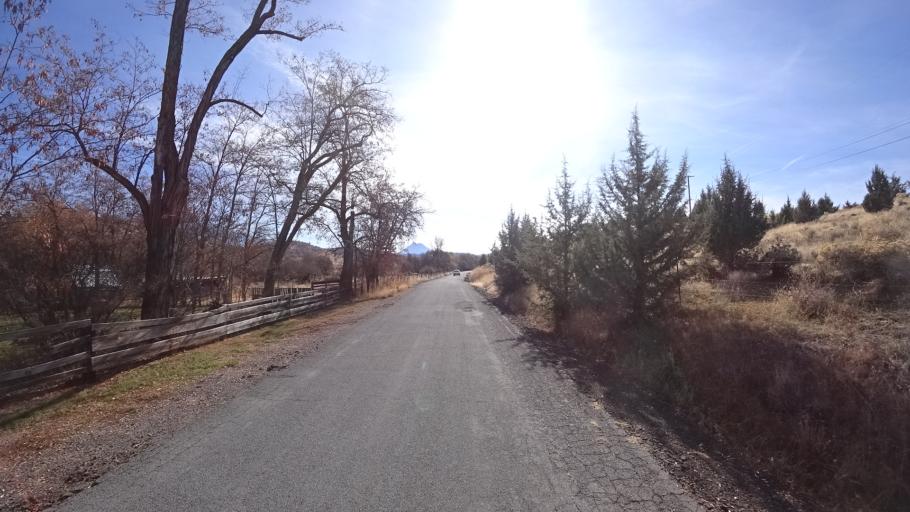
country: US
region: California
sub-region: Siskiyou County
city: Weed
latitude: 41.4777
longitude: -122.4417
